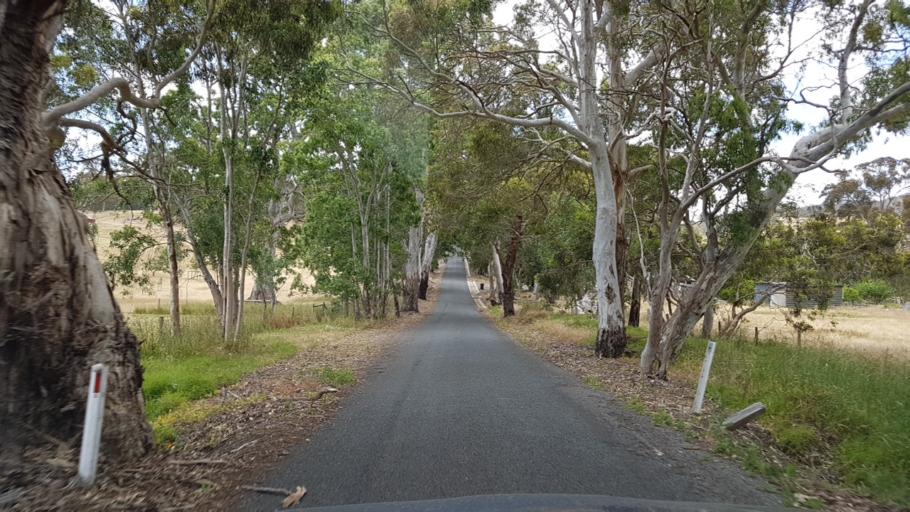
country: AU
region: South Australia
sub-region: Victor Harbor
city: Victor Harbor
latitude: -35.4658
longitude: 138.5945
